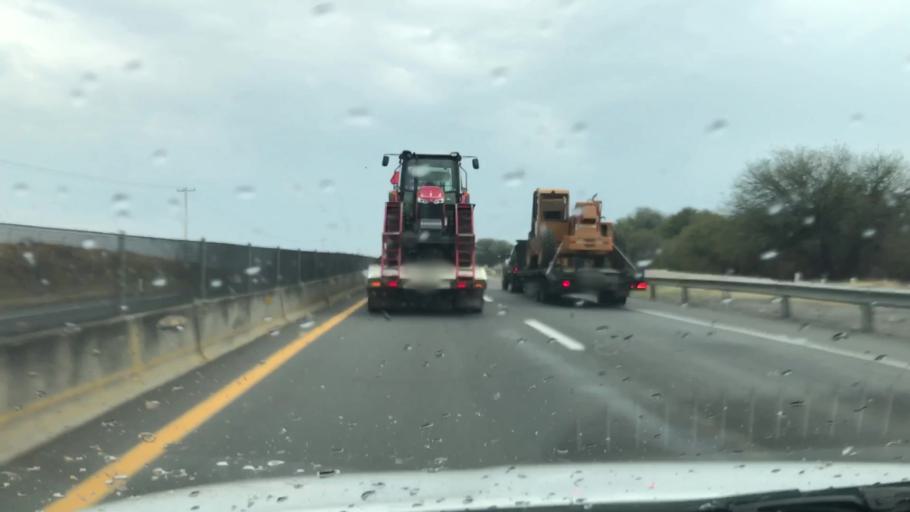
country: MX
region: Jalisco
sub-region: San Juan de los Lagos
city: Mezquitic de la Magdalena
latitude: 21.2176
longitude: -102.3203
